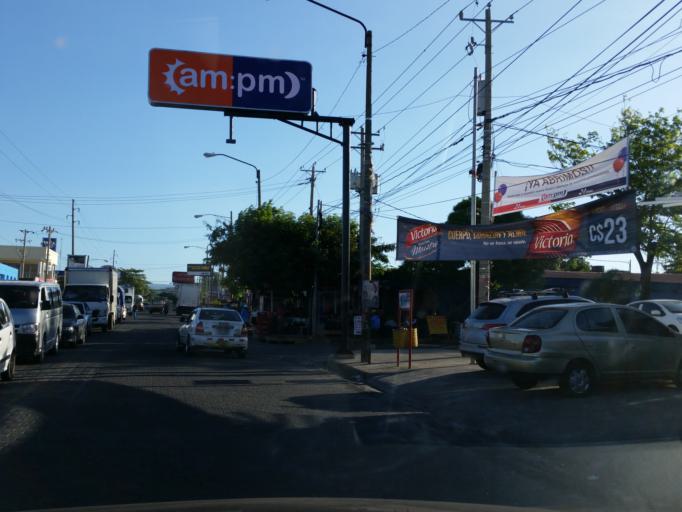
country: NI
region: Managua
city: Ciudad Sandino
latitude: 12.1522
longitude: -86.3046
